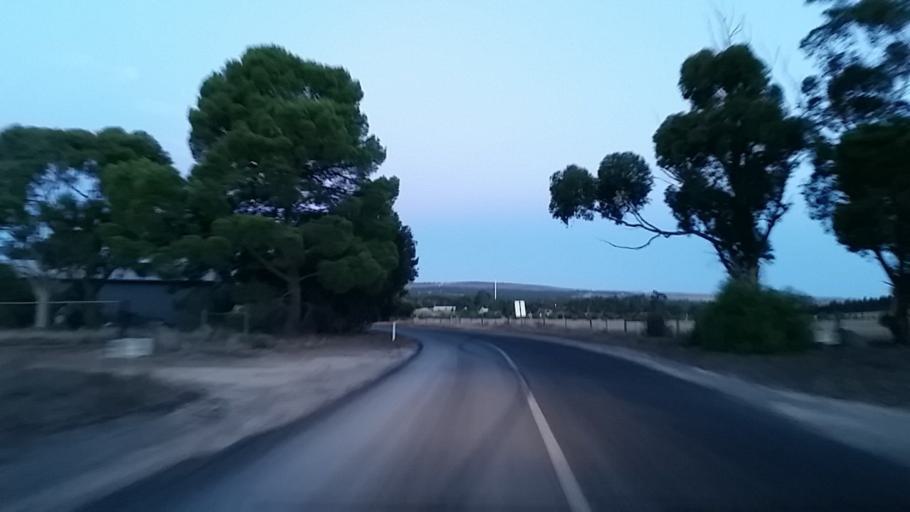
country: AU
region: South Australia
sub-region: Mount Barker
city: Callington
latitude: -35.1081
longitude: 139.0269
